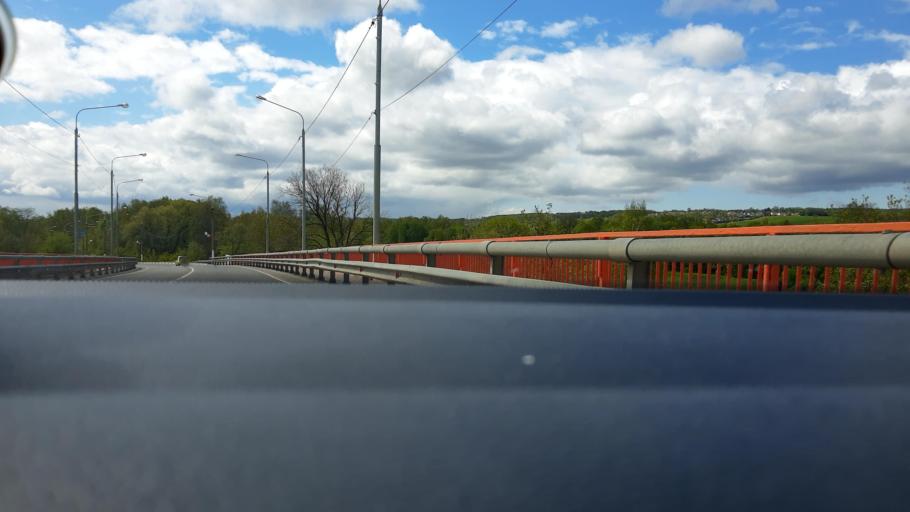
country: RU
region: Moskovskaya
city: Dmitrov
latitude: 56.3258
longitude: 37.4982
